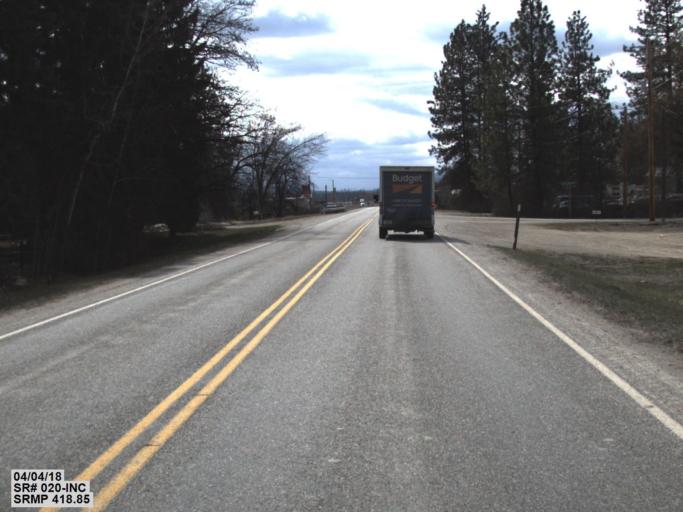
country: US
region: Washington
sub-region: Pend Oreille County
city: Newport
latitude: 48.3400
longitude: -117.3044
